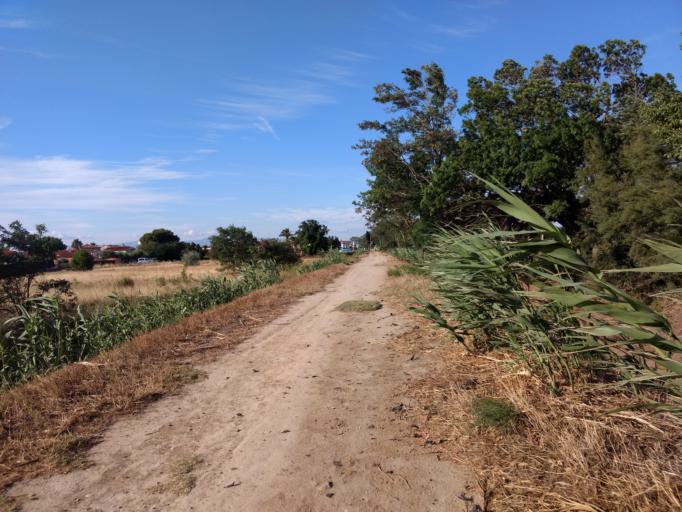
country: FR
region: Languedoc-Roussillon
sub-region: Departement des Pyrenees-Orientales
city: Saint-Laurent-de-la-Salanque
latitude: 42.7785
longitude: 2.9846
